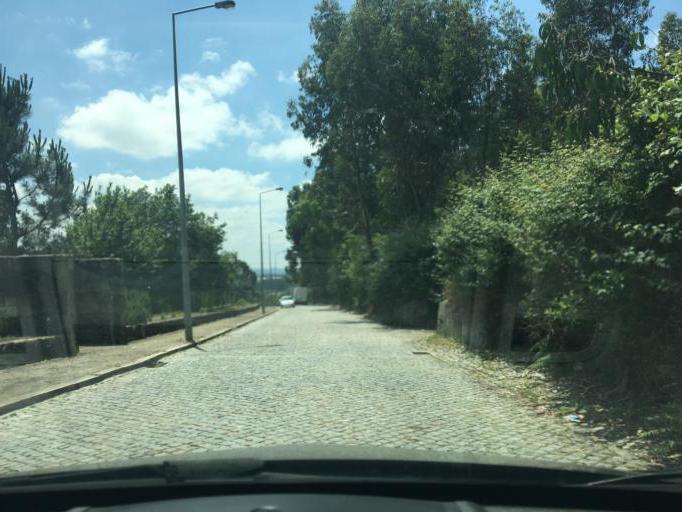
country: PT
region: Porto
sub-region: Maia
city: Anta
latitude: 41.2901
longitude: -8.6145
